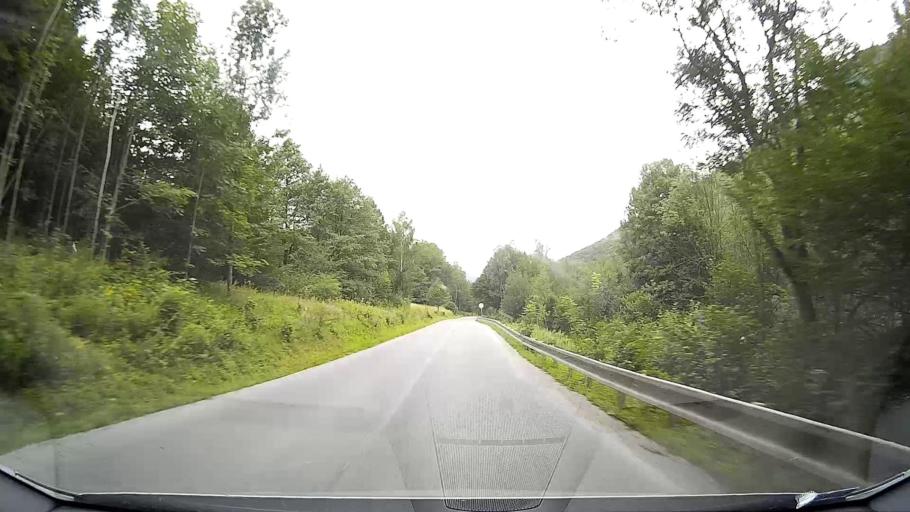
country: SK
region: Banskobystricky
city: Revuca
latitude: 48.7575
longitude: 20.0748
